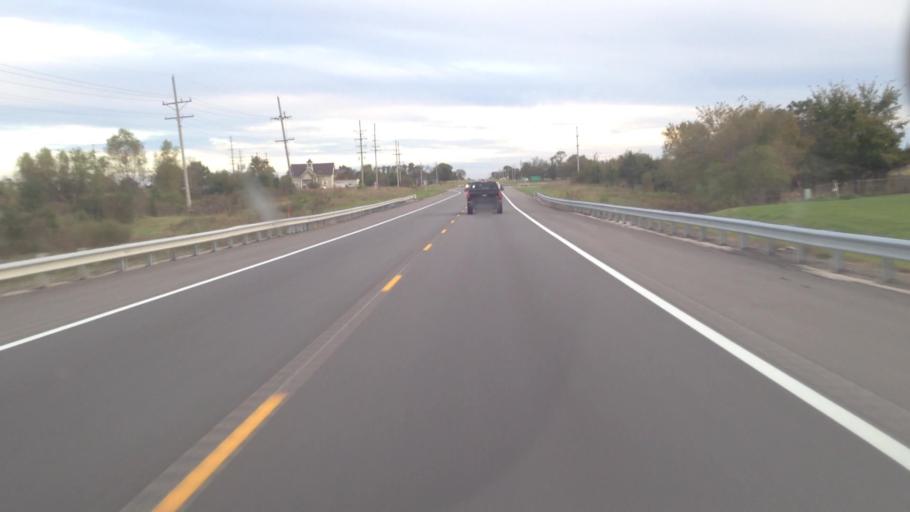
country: US
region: Kansas
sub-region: Franklin County
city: Ottawa
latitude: 38.5528
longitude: -95.2678
